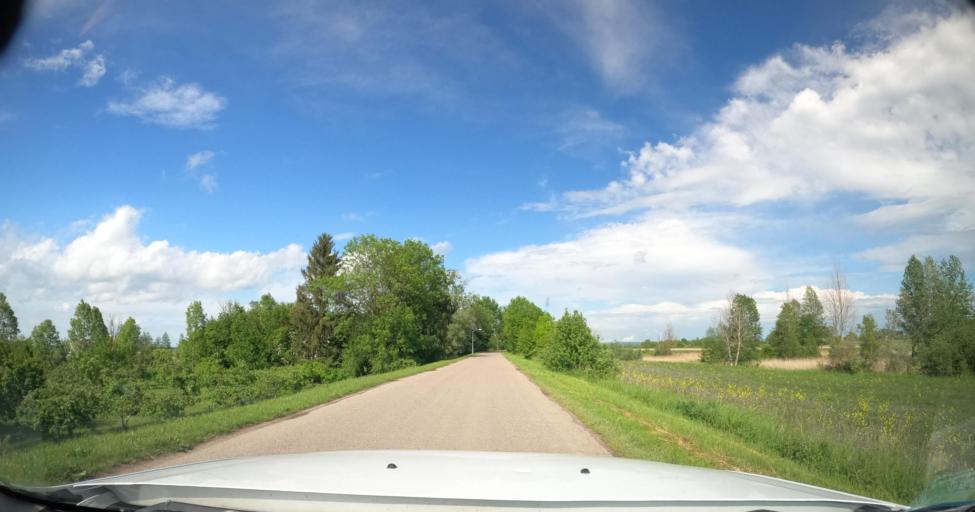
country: PL
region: Warmian-Masurian Voivodeship
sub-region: Powiat elblaski
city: Gronowo Elblaskie
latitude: 54.1760
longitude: 19.2567
